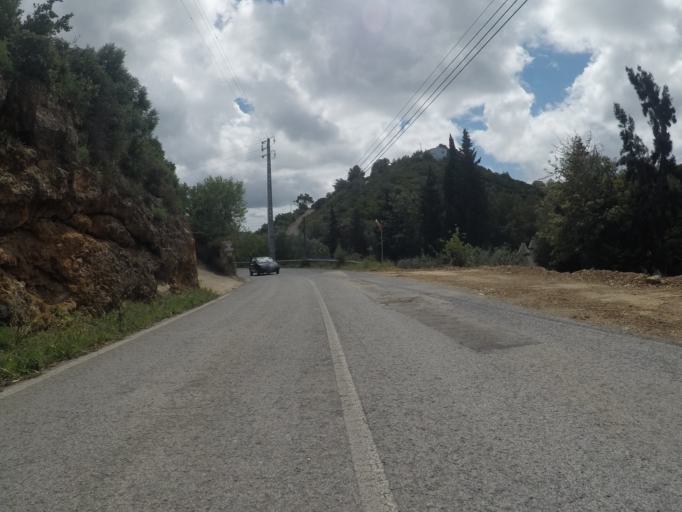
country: PT
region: Faro
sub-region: Vila do Bispo
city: Vila do Bispo
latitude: 37.0724
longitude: -8.8288
